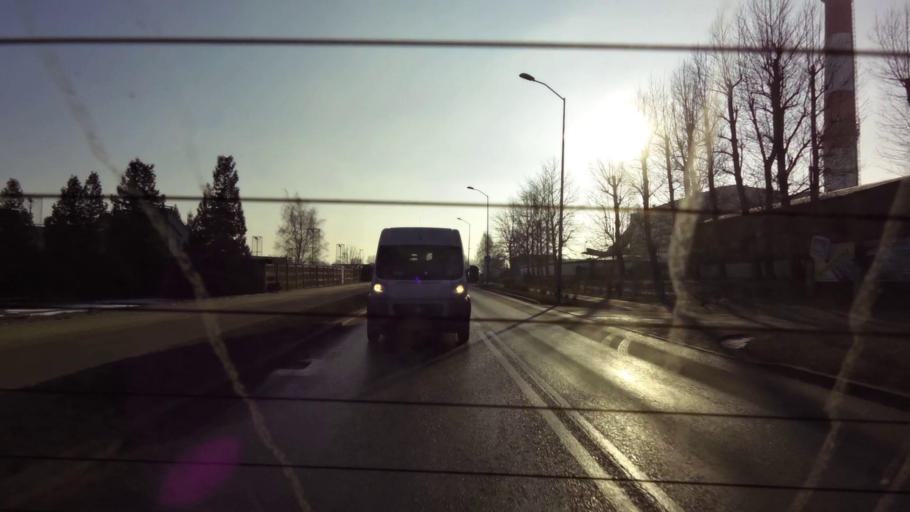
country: PL
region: West Pomeranian Voivodeship
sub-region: Koszalin
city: Koszalin
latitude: 54.1765
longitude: 16.1737
